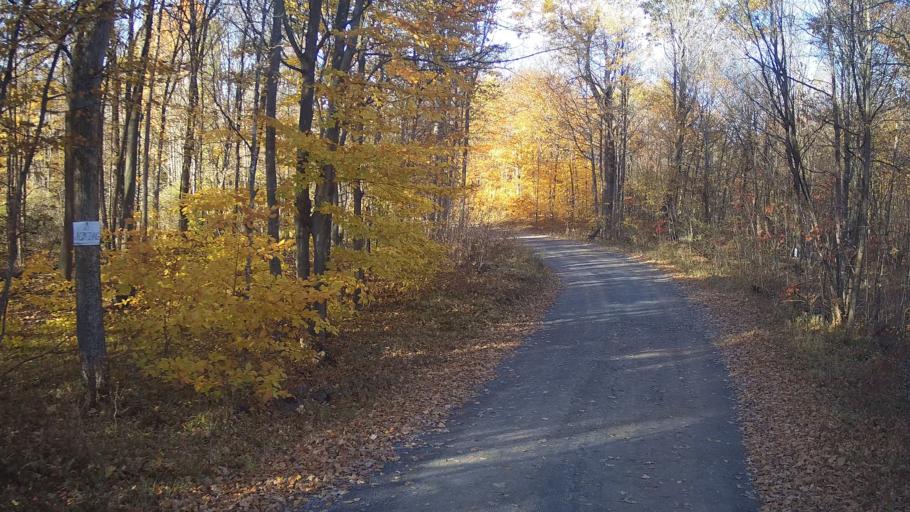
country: CA
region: Ontario
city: Perth
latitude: 44.7274
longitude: -76.4406
